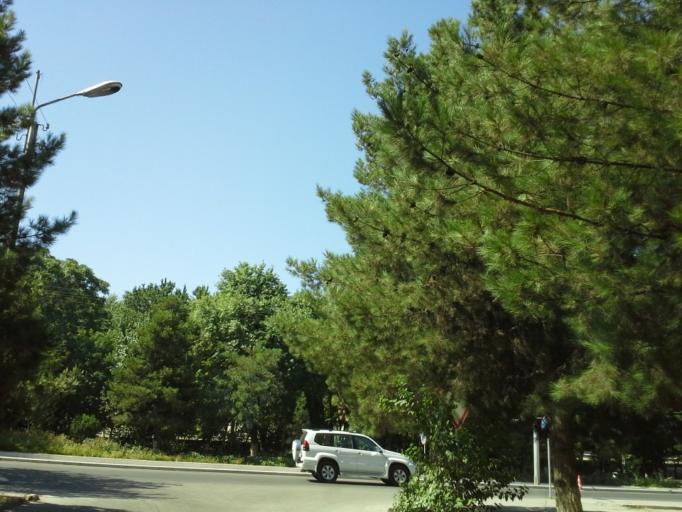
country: TM
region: Ahal
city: Ashgabat
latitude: 37.9467
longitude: 58.3556
